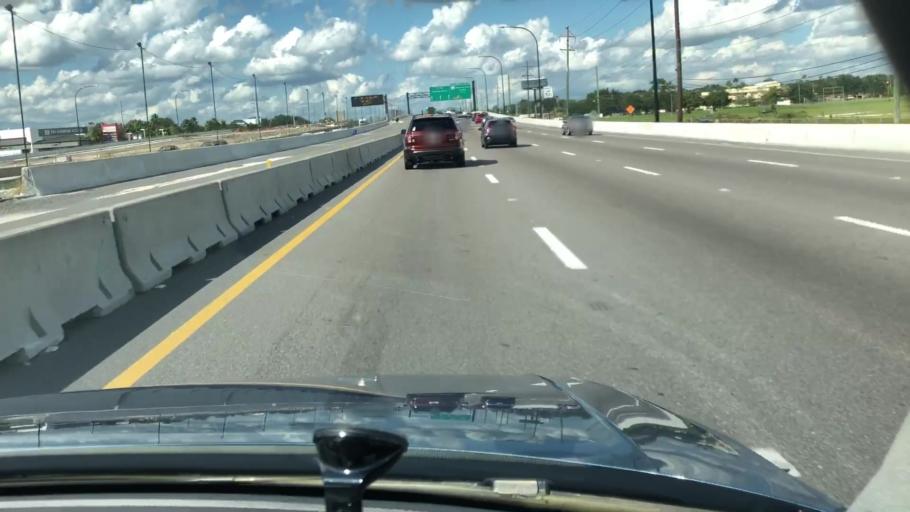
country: US
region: Florida
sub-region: Orange County
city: Eatonville
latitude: 28.6146
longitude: -81.3862
